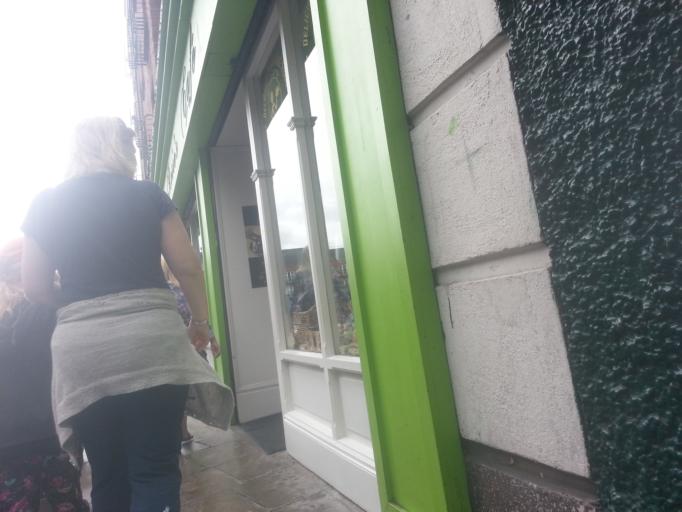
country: IE
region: Leinster
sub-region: Dublin City
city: Dublin
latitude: 53.3430
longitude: -6.2700
